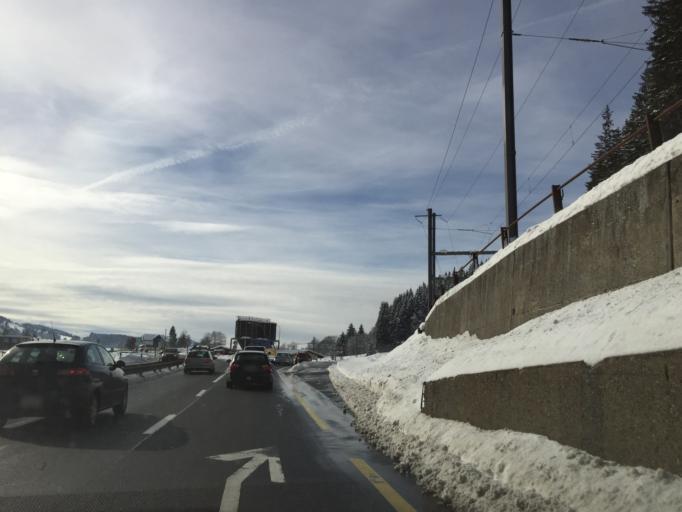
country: CH
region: Schwyz
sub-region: Bezirk Hoefe
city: Schindellegi
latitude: 47.1589
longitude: 8.7256
